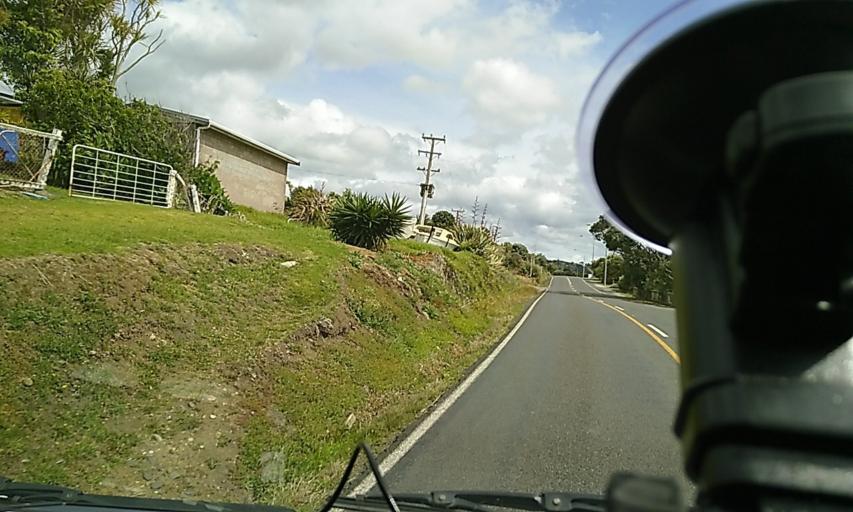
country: NZ
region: Northland
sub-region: Far North District
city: Ahipara
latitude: -35.5125
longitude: 173.3890
